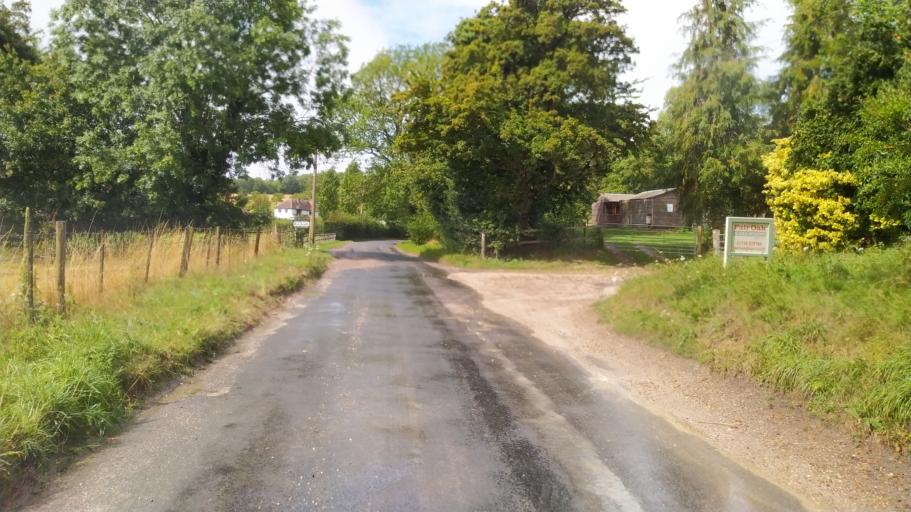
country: GB
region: England
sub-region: Hampshire
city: Swanmore
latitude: 51.0063
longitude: -1.1249
